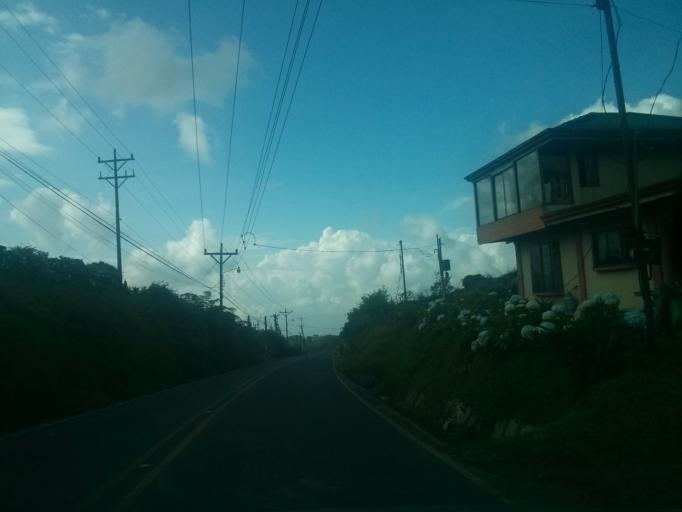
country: CR
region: Heredia
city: Santo Domingo
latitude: 10.1659
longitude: -84.1559
